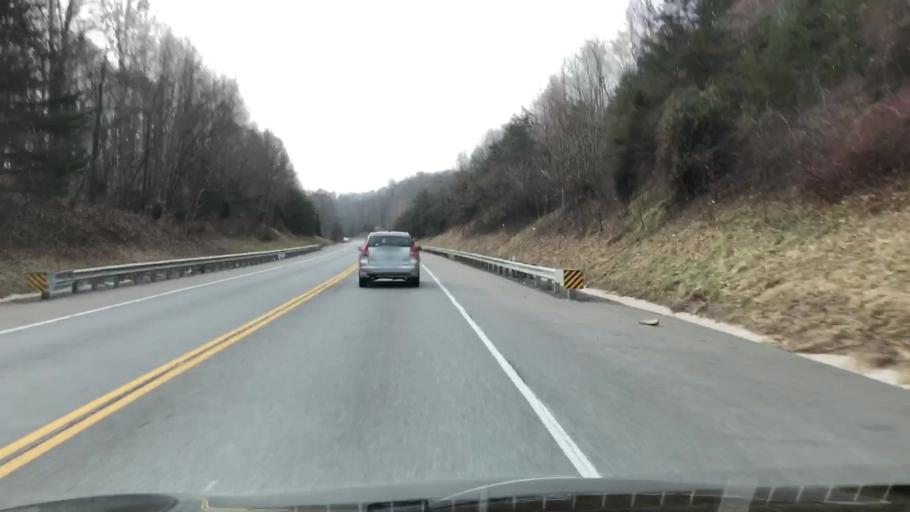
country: US
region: Virginia
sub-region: City of Lynchburg
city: West Lynchburg
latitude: 37.4359
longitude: -79.2354
